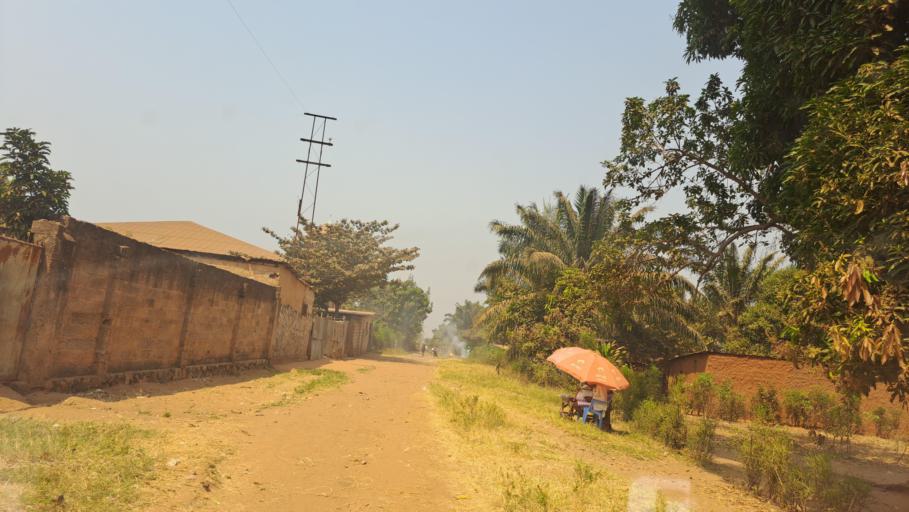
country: CD
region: Kasai-Oriental
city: Mbuji-Mayi
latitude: -6.1253
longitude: 23.6120
